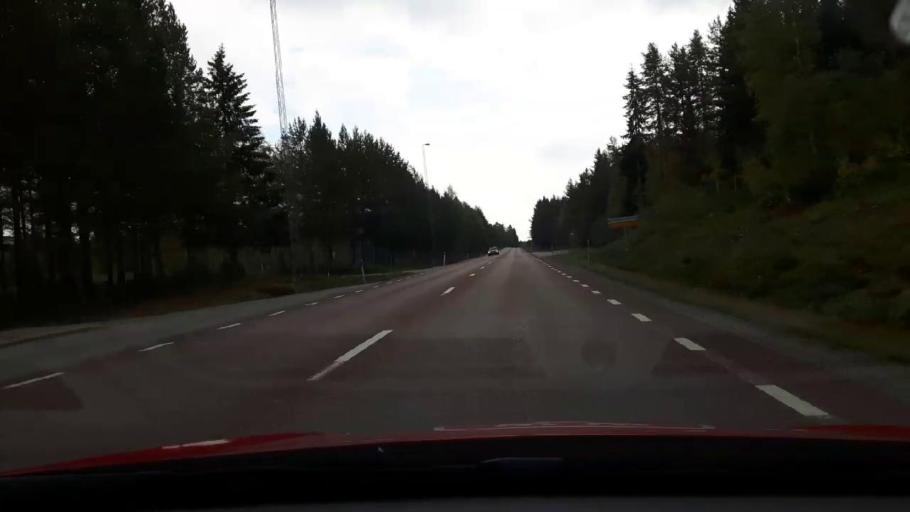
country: SE
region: Gaevleborg
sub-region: Bollnas Kommun
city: Kilafors
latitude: 61.2675
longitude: 16.5443
